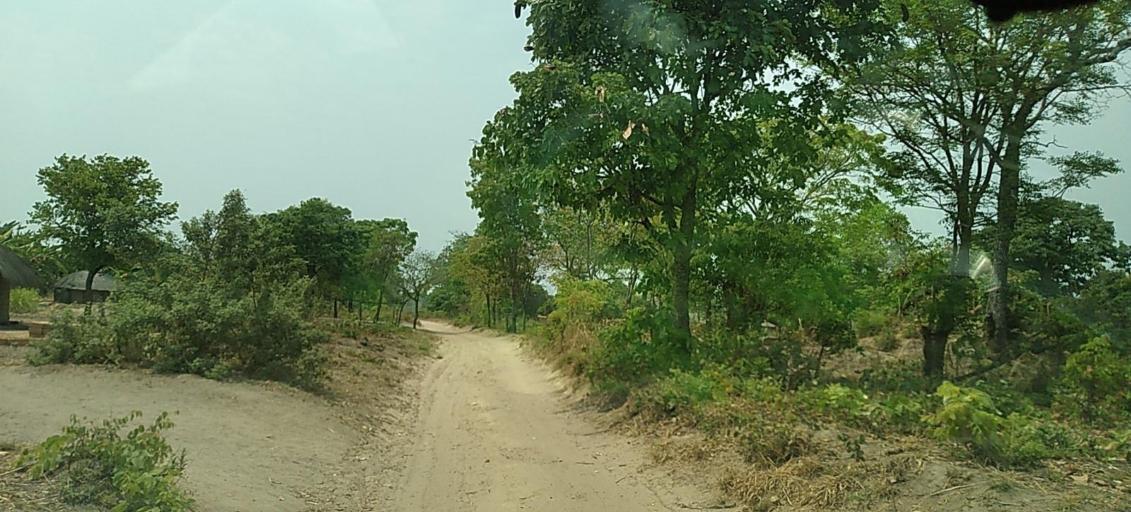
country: ZM
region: North-Western
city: Kabompo
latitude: -13.4733
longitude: 24.4503
